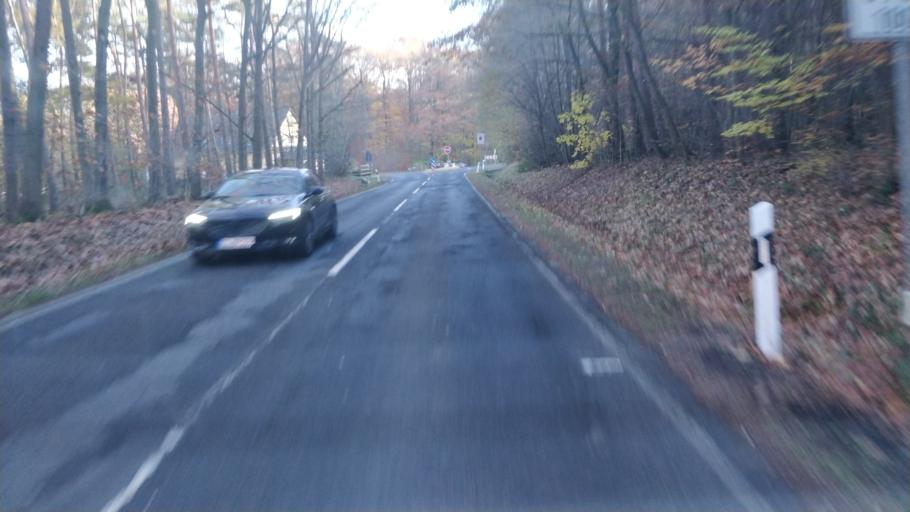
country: DE
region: North Rhine-Westphalia
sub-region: Regierungsbezirk Koln
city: Rheinbach
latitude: 50.6149
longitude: 6.9129
